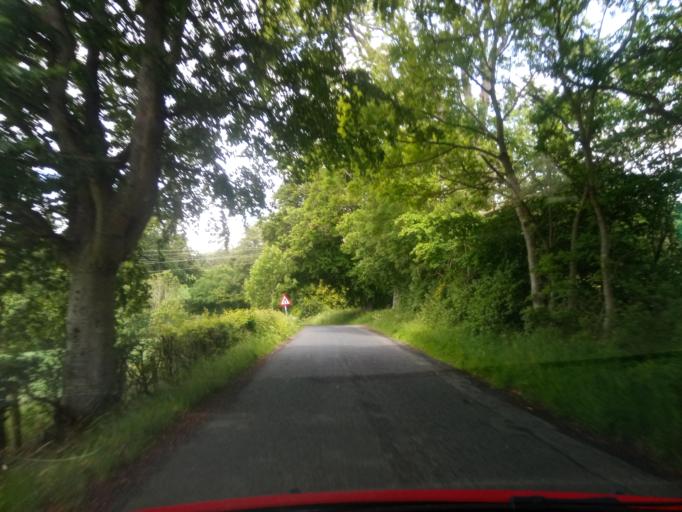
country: GB
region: Scotland
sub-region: The Scottish Borders
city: Selkirk
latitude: 55.5851
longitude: -2.8397
